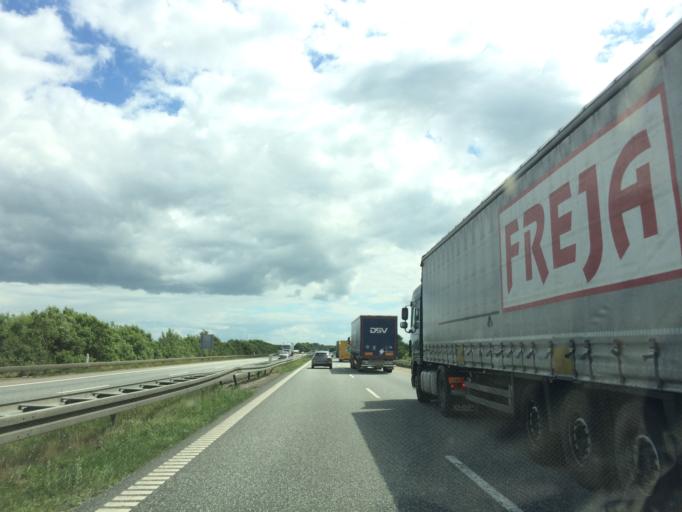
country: DK
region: North Denmark
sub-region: Mariagerfjord Kommune
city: Hobro
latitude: 56.7235
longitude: 9.7162
